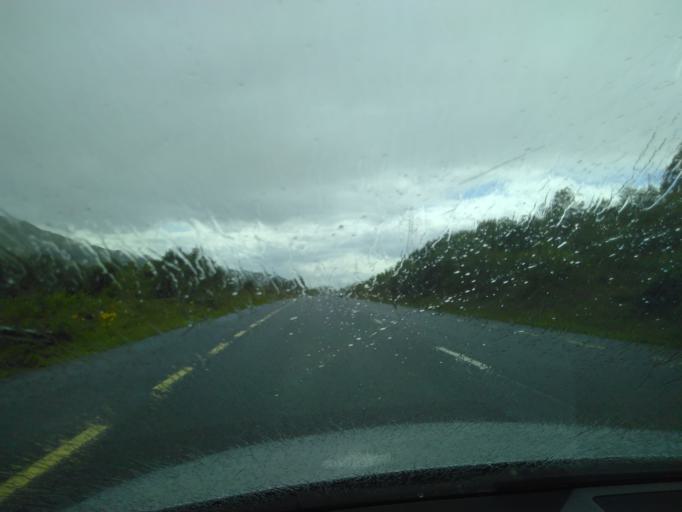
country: IE
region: Ulster
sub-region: County Donegal
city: Donegal
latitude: 54.7135
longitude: -7.9647
